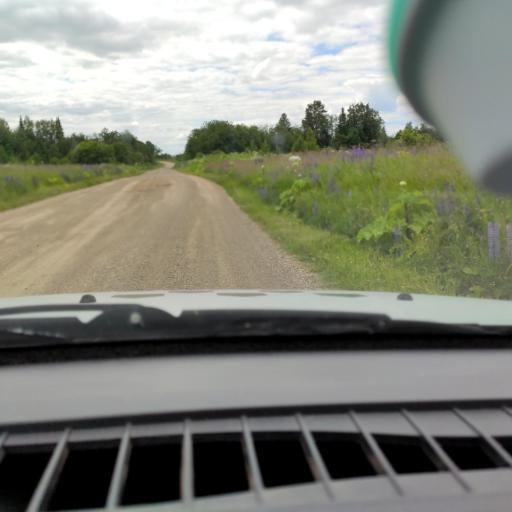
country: RU
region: Perm
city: Suksun
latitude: 57.1938
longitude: 57.5746
